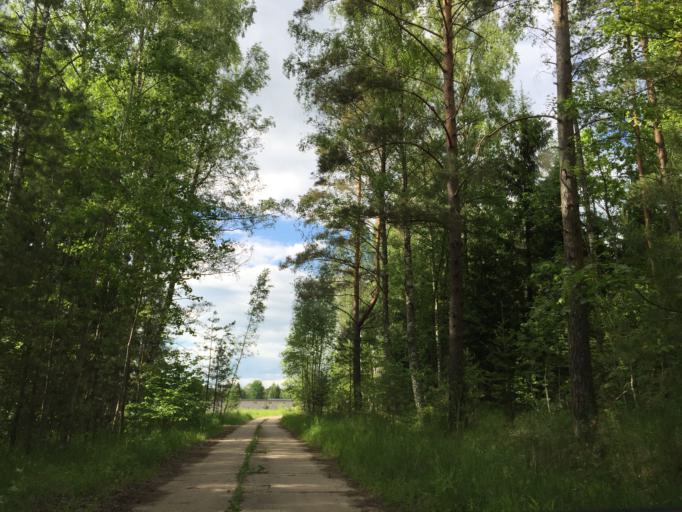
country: LV
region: Dobeles Rajons
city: Dobele
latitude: 56.6394
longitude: 23.1749
